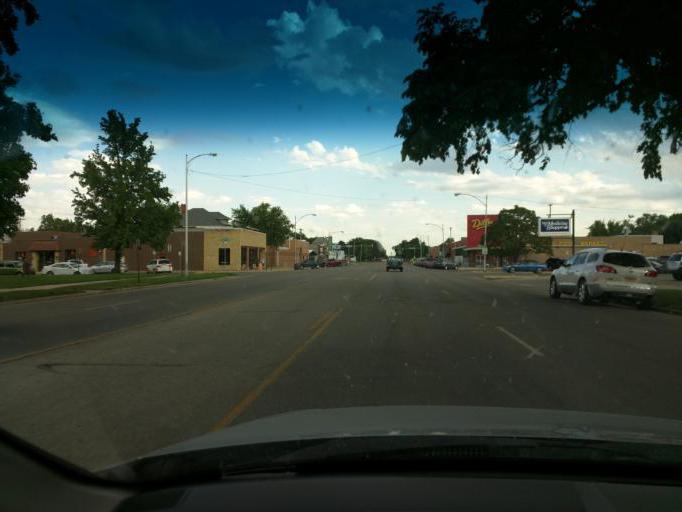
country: US
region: Kansas
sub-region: Reno County
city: Hutchinson
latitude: 38.0692
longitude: -97.9319
